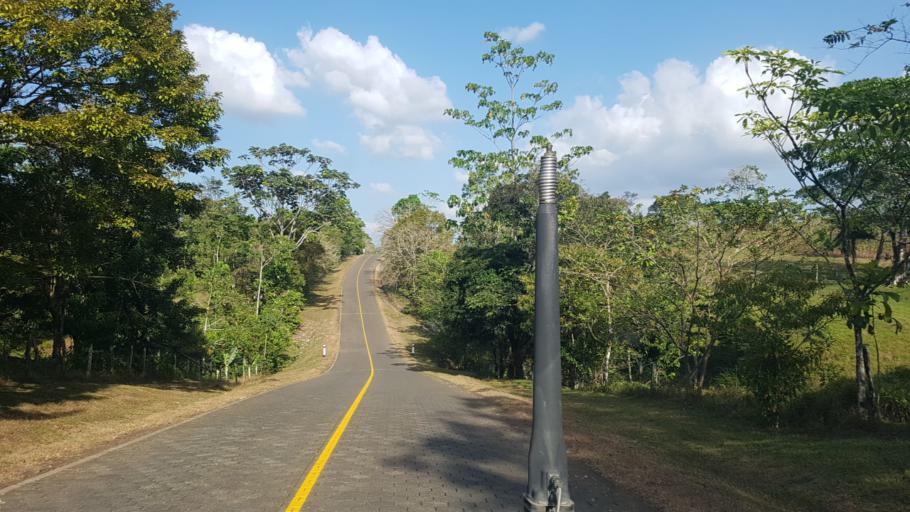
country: NI
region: Atlantico Sur
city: Nueva Guinea
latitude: 11.6905
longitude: -84.4215
